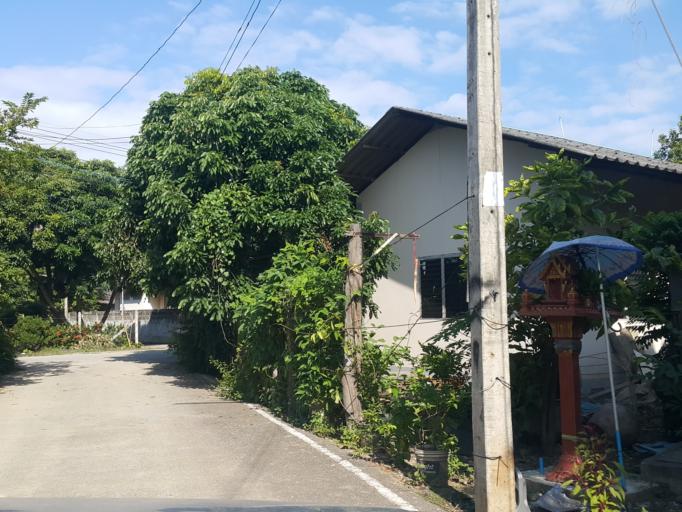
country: TH
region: Chiang Mai
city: Saraphi
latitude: 18.7424
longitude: 99.0527
